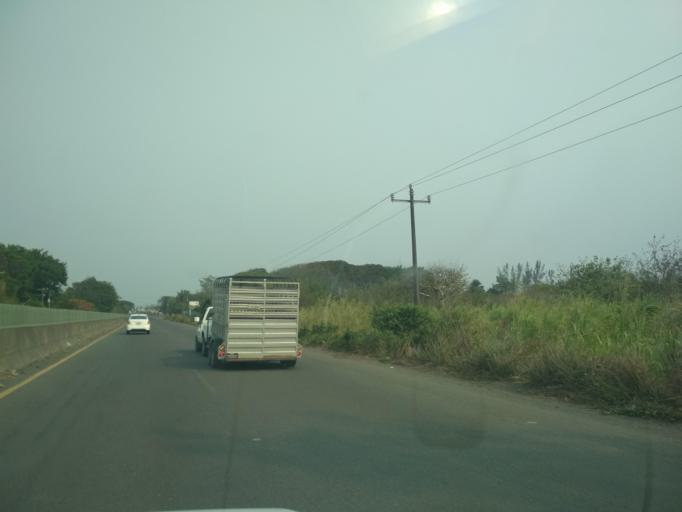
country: MX
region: Veracruz
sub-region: Veracruz
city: Hacienda Sotavento
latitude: 19.1020
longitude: -96.2167
